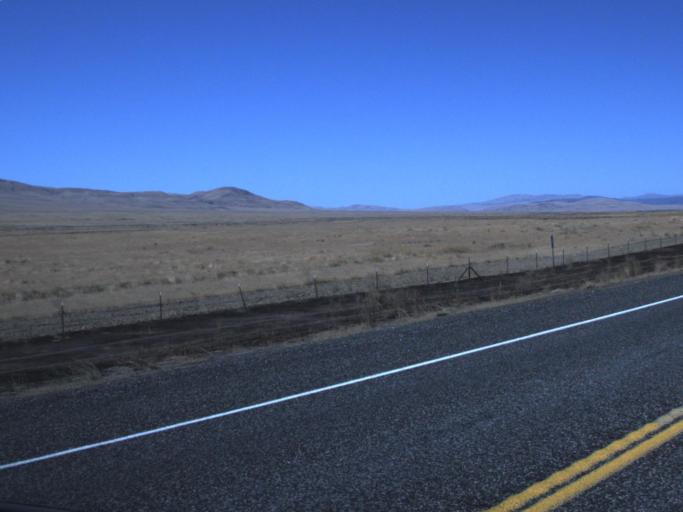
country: US
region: Washington
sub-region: Benton County
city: Benton City
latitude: 46.4449
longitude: -119.4952
